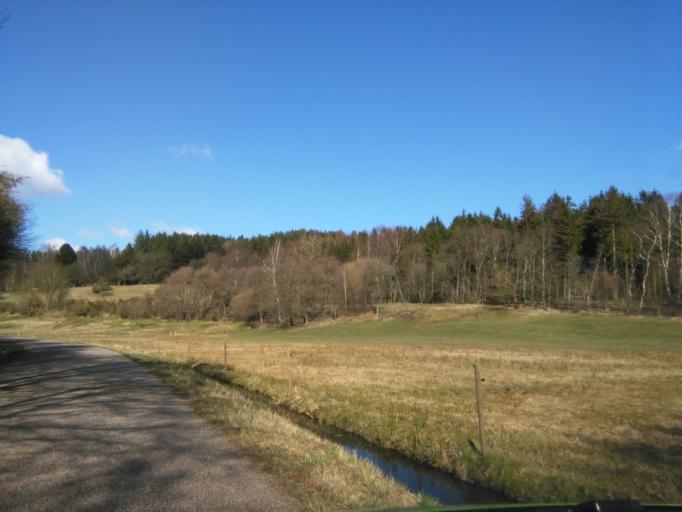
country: DK
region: Central Jutland
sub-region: Skanderborg Kommune
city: Ry
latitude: 56.1017
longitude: 9.7409
